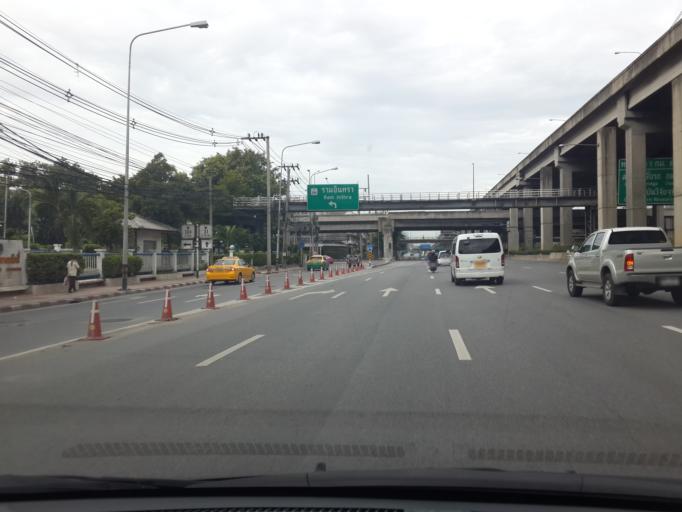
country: TH
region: Bangkok
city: Lak Si
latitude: 13.8855
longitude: 100.5825
